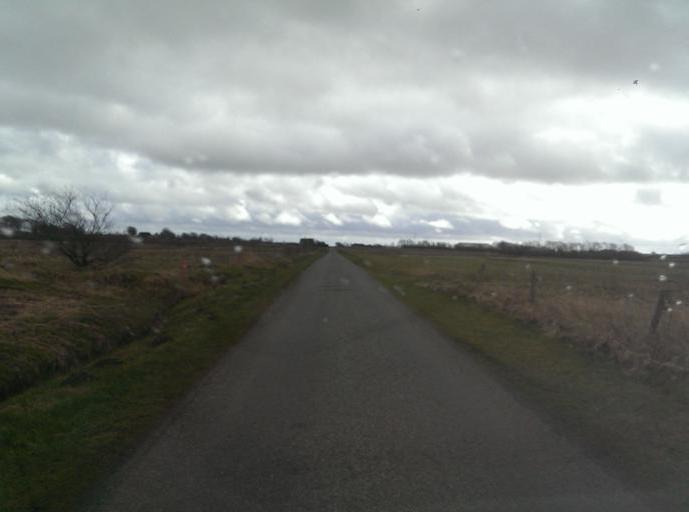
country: DK
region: South Denmark
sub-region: Esbjerg Kommune
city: Bramming
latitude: 55.4415
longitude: 8.6779
